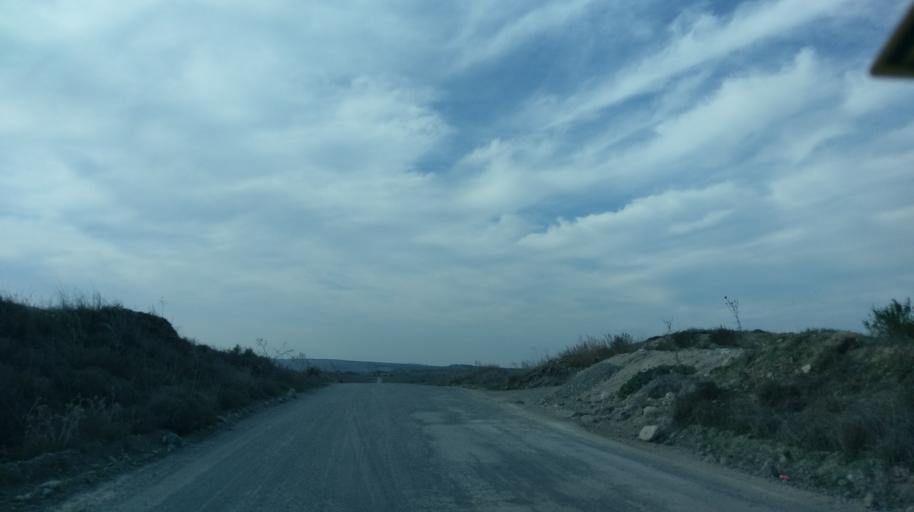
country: CY
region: Keryneia
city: Lapithos
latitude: 35.2852
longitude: 33.1532
